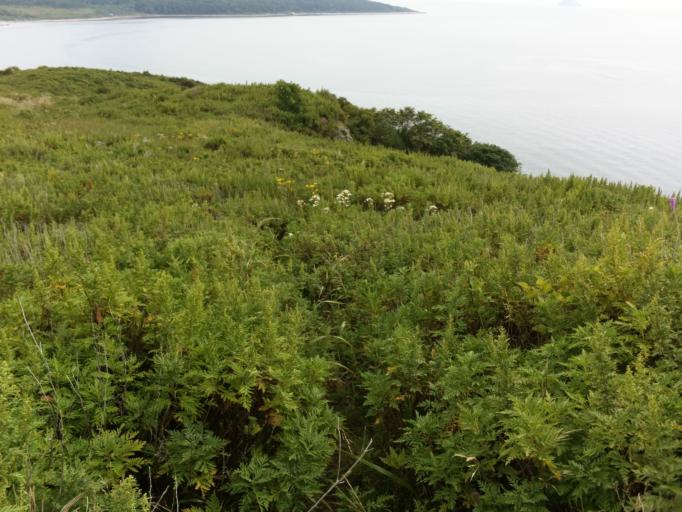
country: RU
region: Primorskiy
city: Popova
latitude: 42.9209
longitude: 131.7111
